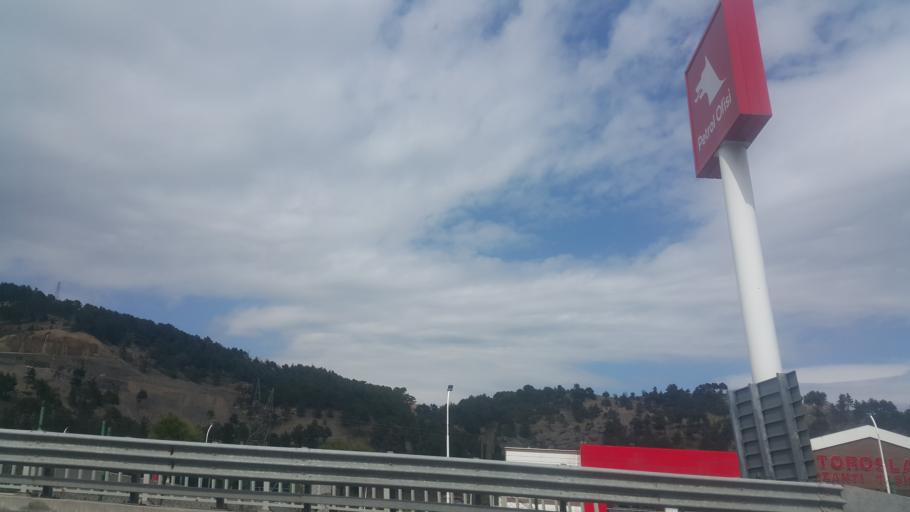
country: TR
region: Adana
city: Pozanti
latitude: 37.4623
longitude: 34.8764
